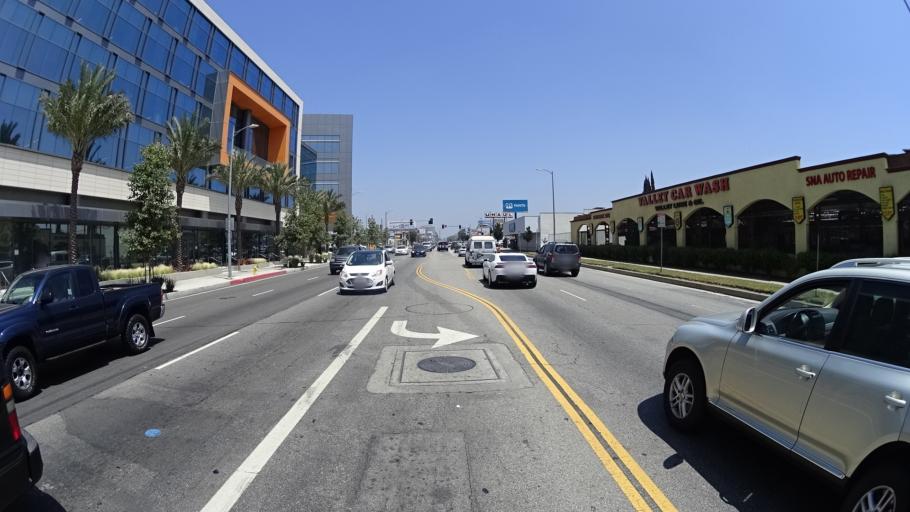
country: US
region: California
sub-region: Los Angeles County
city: Van Nuys
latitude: 34.2074
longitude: -118.4488
